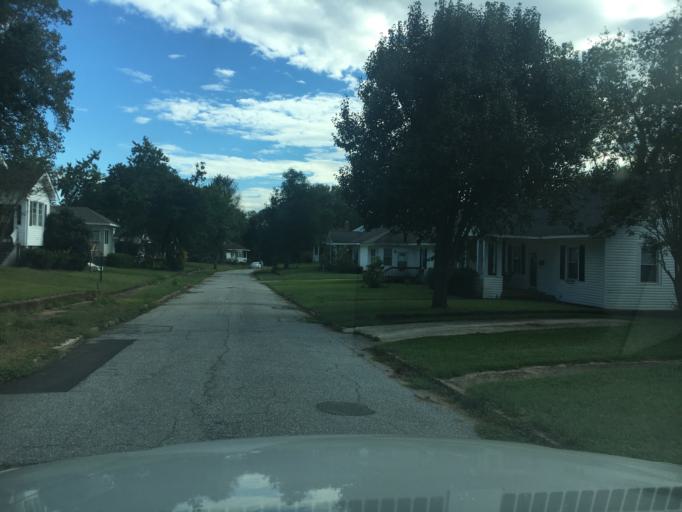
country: US
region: South Carolina
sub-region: Spartanburg County
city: Lyman
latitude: 34.9452
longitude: -82.1287
